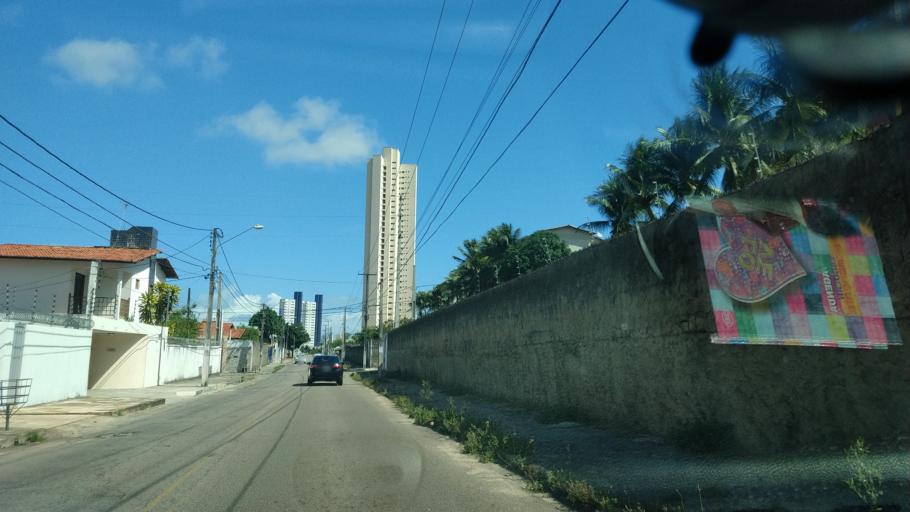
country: BR
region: Rio Grande do Norte
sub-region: Natal
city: Natal
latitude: -5.8677
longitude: -35.1963
